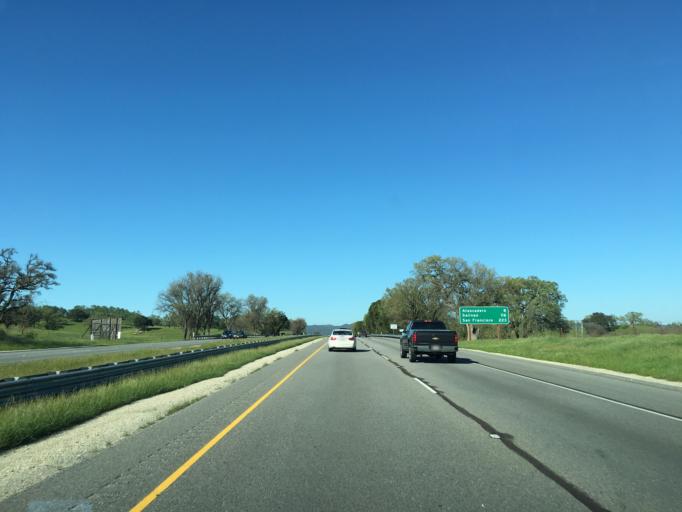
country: US
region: California
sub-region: San Luis Obispo County
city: Santa Margarita
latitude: 35.3876
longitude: -120.6273
